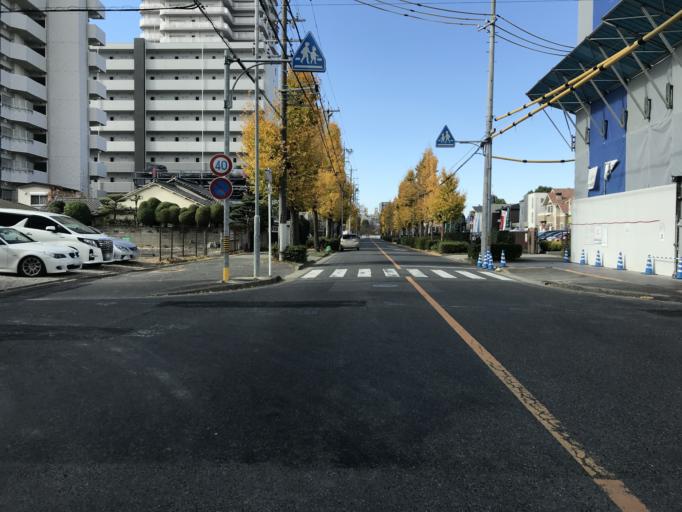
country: JP
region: Aichi
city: Nagoya-shi
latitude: 35.1969
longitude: 136.9193
